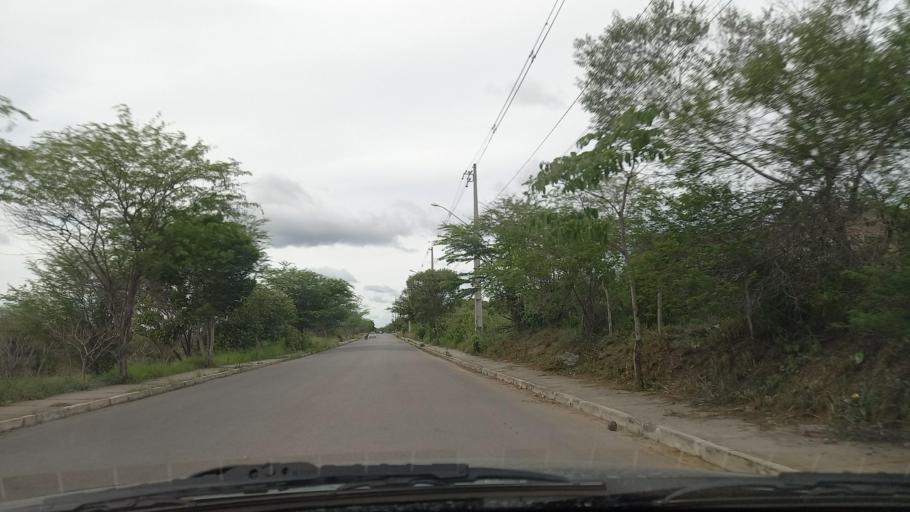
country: BR
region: Pernambuco
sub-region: Gravata
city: Gravata
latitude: -8.2098
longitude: -35.5966
